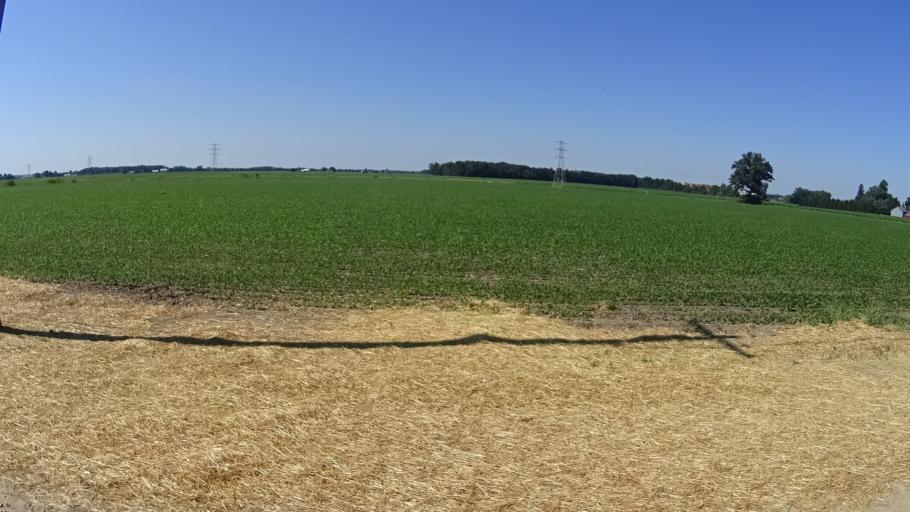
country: US
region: Ohio
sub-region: Erie County
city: Huron
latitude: 41.3930
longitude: -82.6292
